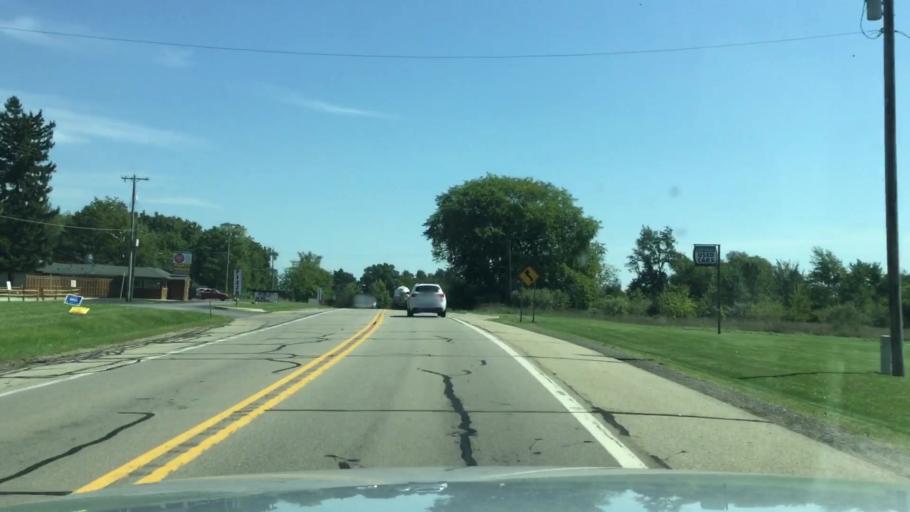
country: US
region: Michigan
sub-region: Washtenaw County
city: Manchester
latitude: 42.0715
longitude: -84.0900
